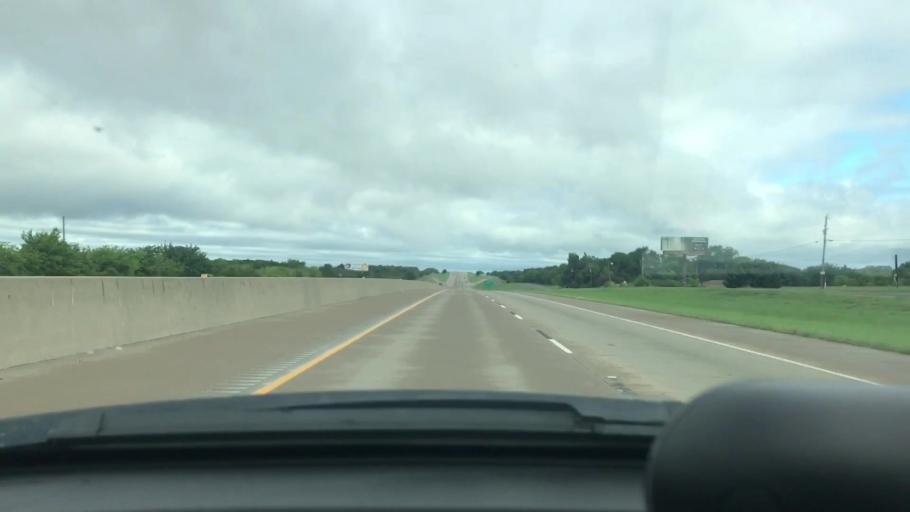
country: US
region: Texas
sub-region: Grayson County
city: Van Alstyne
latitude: 33.4522
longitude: -96.6056
